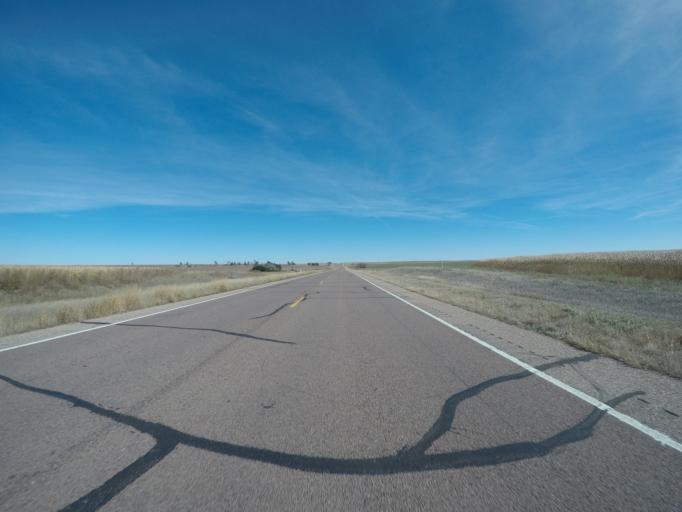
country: US
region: Colorado
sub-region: Kit Carson County
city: Burlington
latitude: 39.6580
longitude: -102.5219
